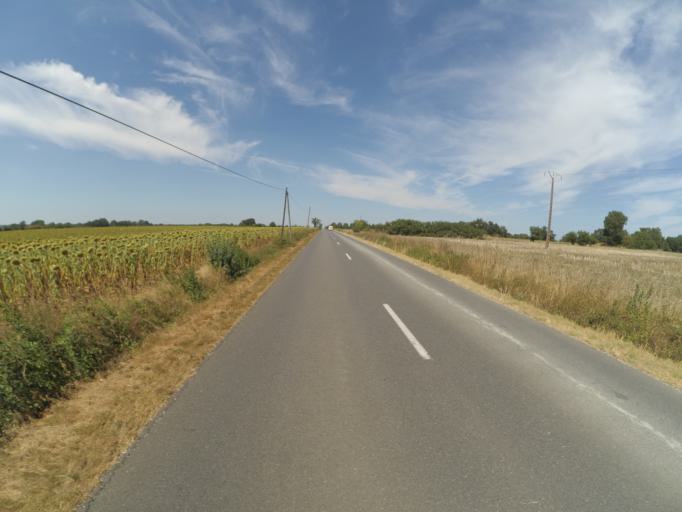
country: FR
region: Poitou-Charentes
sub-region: Departement de la Vienne
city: Availles-Limouzine
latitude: 46.1641
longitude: 0.5488
